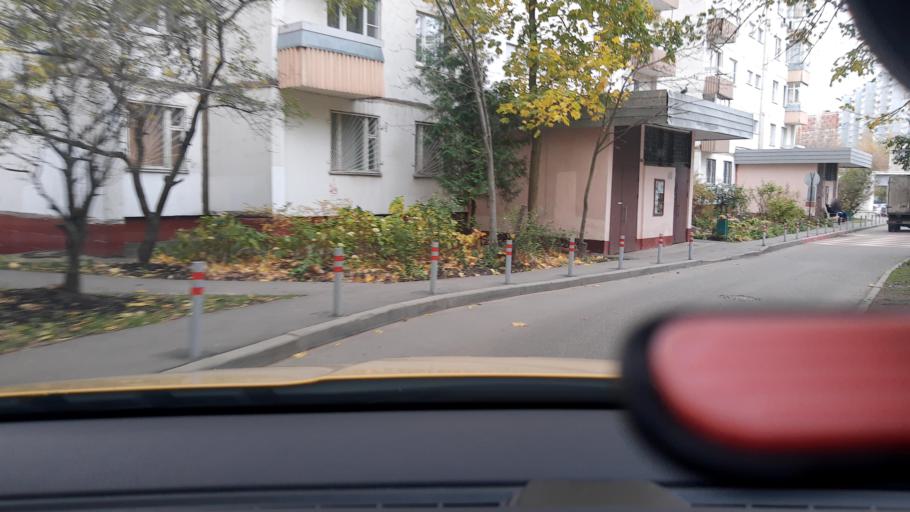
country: RU
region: Moscow
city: Solntsevo
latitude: 55.6504
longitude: 37.3955
